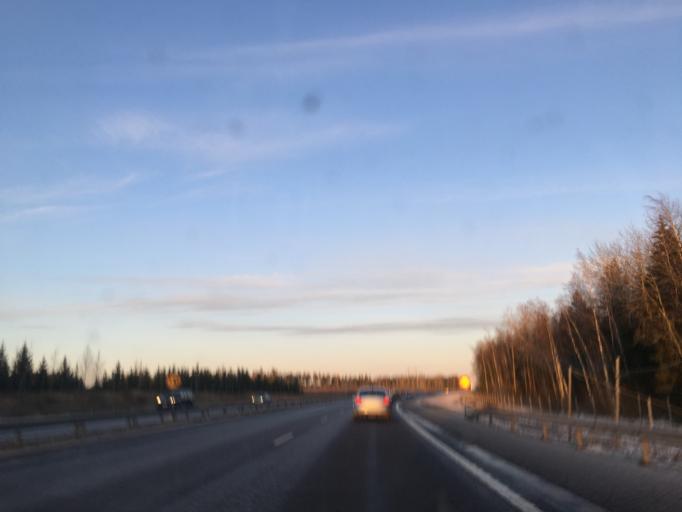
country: FI
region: Varsinais-Suomi
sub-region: Turku
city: Vahto
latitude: 60.5358
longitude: 22.3128
